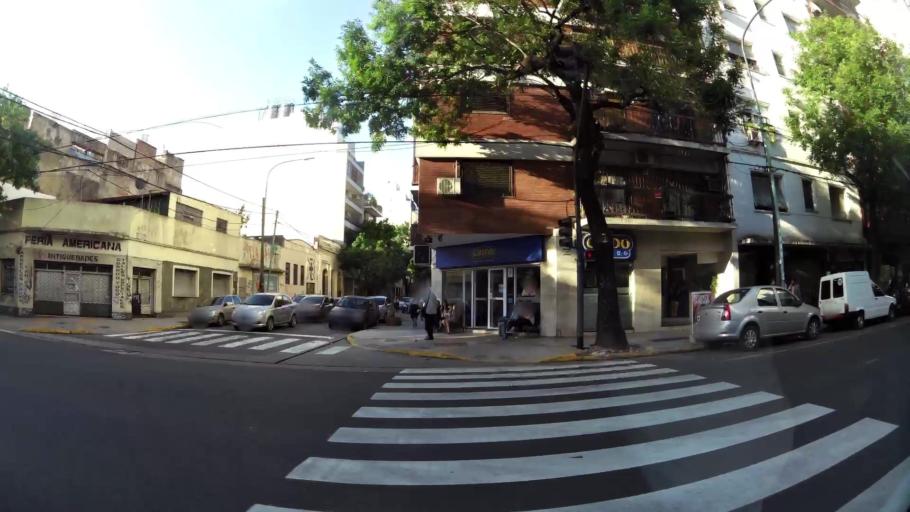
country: AR
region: Buenos Aires F.D.
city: Colegiales
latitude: -34.6086
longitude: -58.4229
